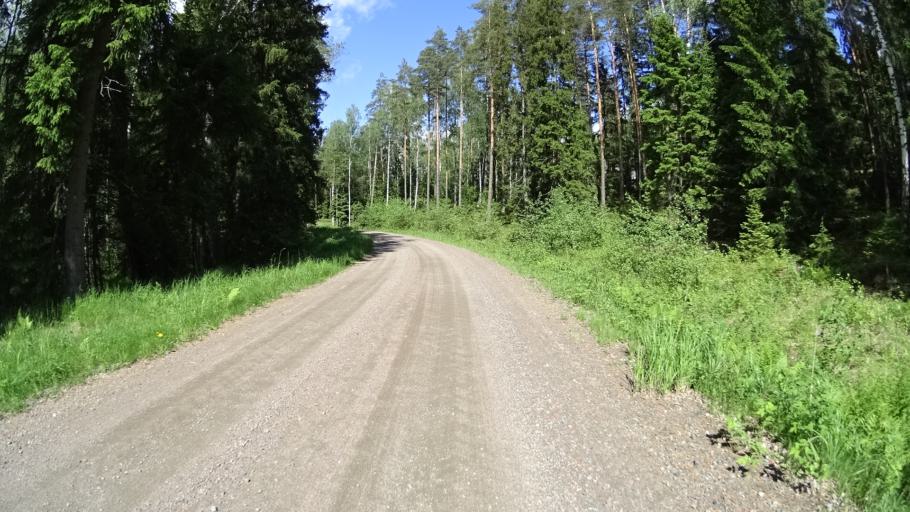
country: FI
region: Uusimaa
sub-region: Raaseporin
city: Karis
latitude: 60.1324
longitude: 23.6199
